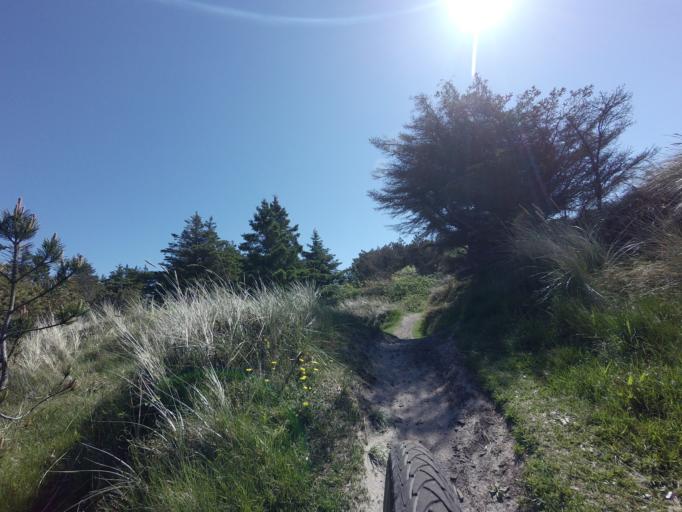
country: DK
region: North Denmark
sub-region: Jammerbugt Kommune
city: Pandrup
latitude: 57.3014
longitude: 9.6519
